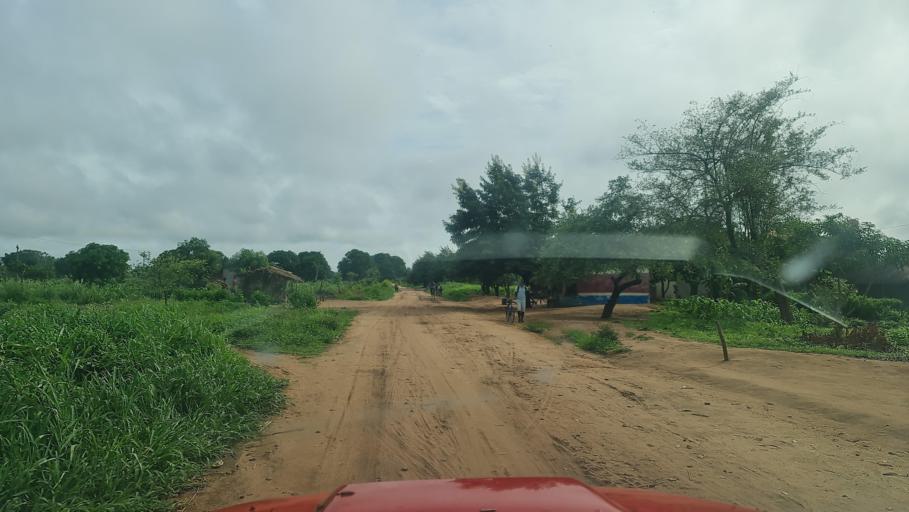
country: MW
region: Southern Region
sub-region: Nsanje District
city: Nsanje
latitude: -17.2868
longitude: 35.6078
